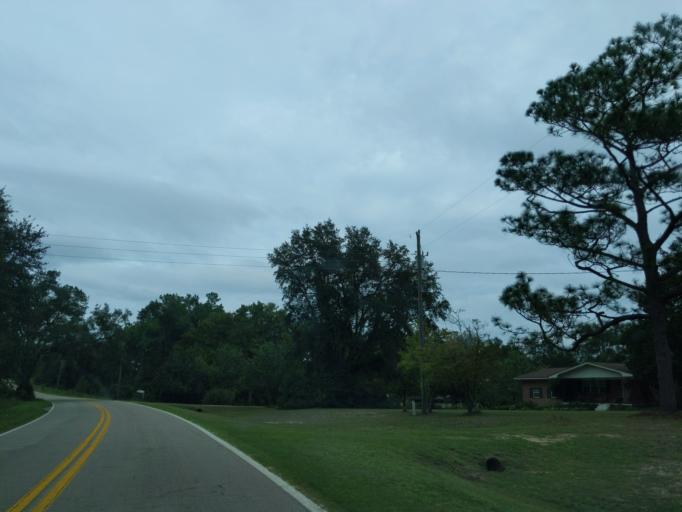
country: US
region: Florida
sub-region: Gadsden County
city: Midway
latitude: 30.4321
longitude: -84.4131
